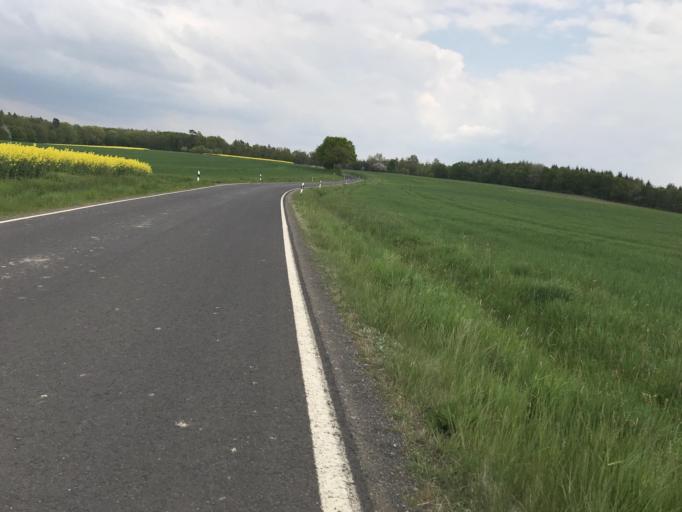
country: DE
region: Hesse
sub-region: Regierungsbezirk Giessen
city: Laubach
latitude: 50.5288
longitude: 8.9963
